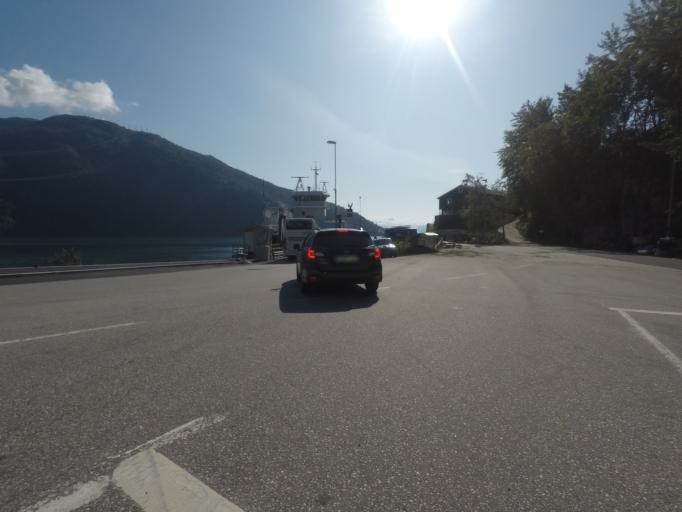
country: NO
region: Sogn og Fjordane
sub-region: Balestrand
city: Balestrand
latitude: 61.2150
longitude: 6.5650
